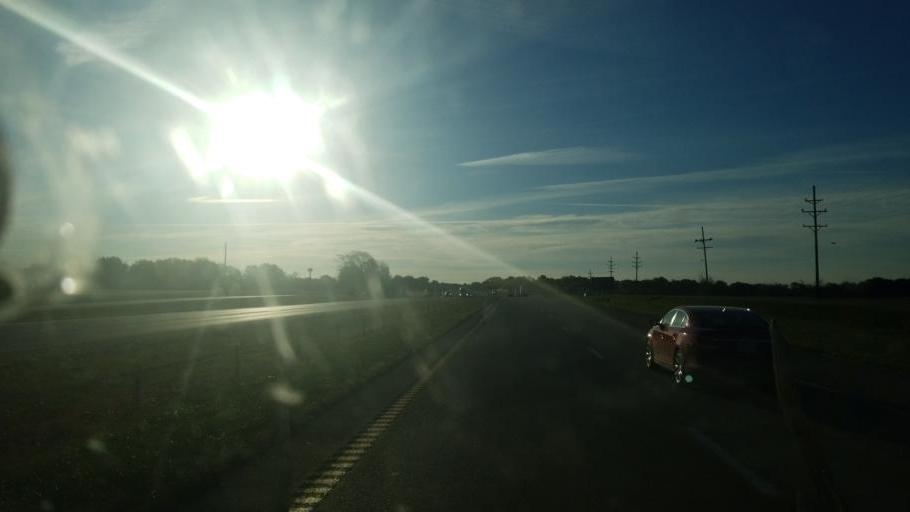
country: US
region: Missouri
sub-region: Warren County
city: Warrenton
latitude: 38.8352
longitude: -91.2204
